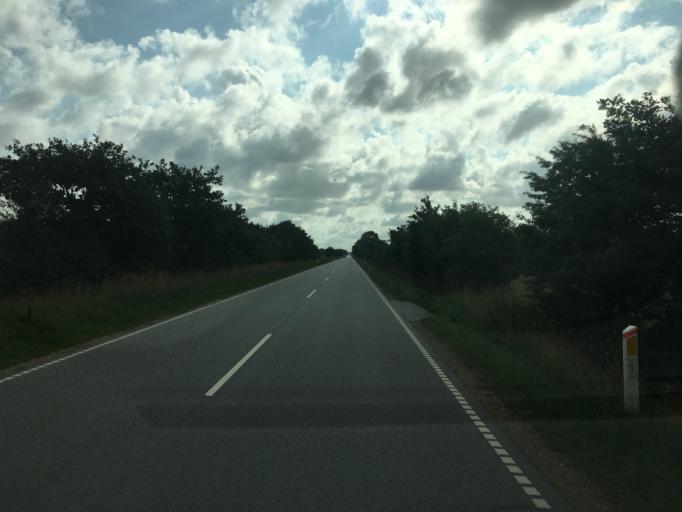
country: DK
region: South Denmark
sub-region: Tonder Kommune
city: Sherrebek
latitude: 55.1235
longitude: 8.8221
